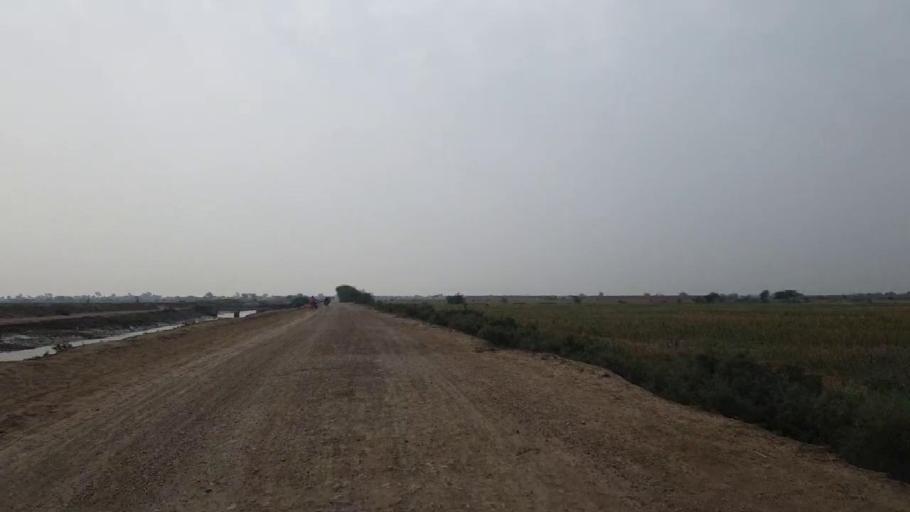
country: PK
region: Sindh
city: Kario
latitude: 24.8925
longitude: 68.5262
